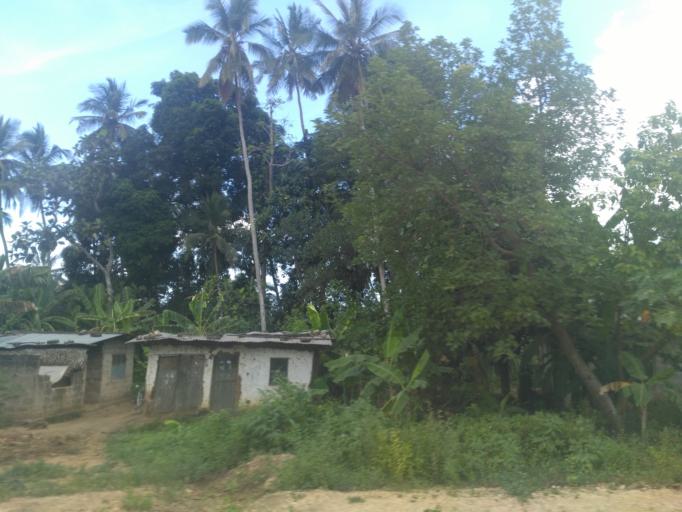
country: TZ
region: Zanzibar North
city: Gamba
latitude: -5.9738
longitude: 39.2997
